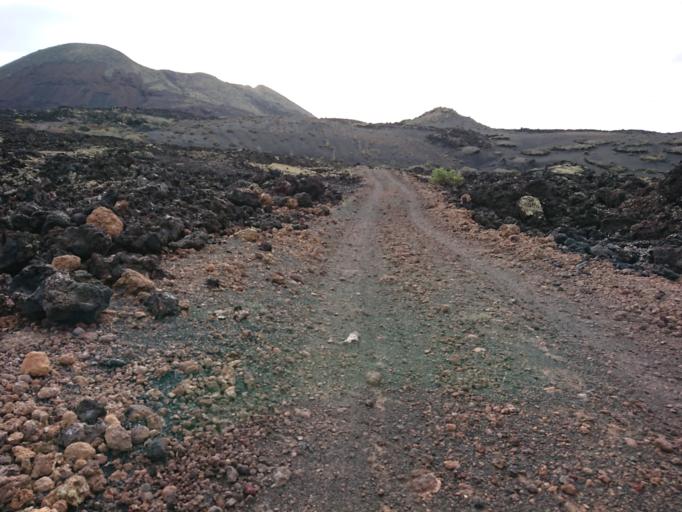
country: ES
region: Canary Islands
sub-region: Provincia de Las Palmas
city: Tinajo
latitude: 29.0144
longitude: -13.6775
